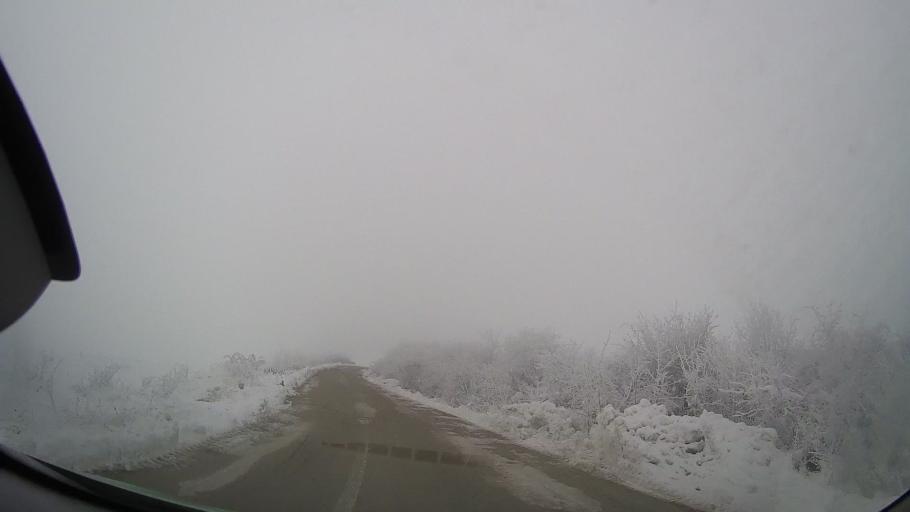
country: RO
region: Iasi
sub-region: Comuna Dagata
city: Dagata
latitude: 46.9224
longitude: 27.1752
